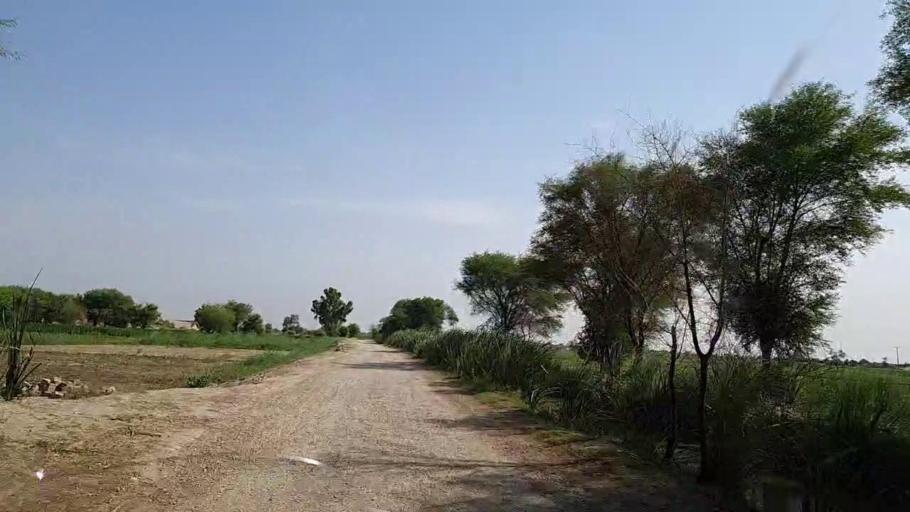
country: PK
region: Sindh
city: Khanpur
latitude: 27.7221
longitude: 69.3605
